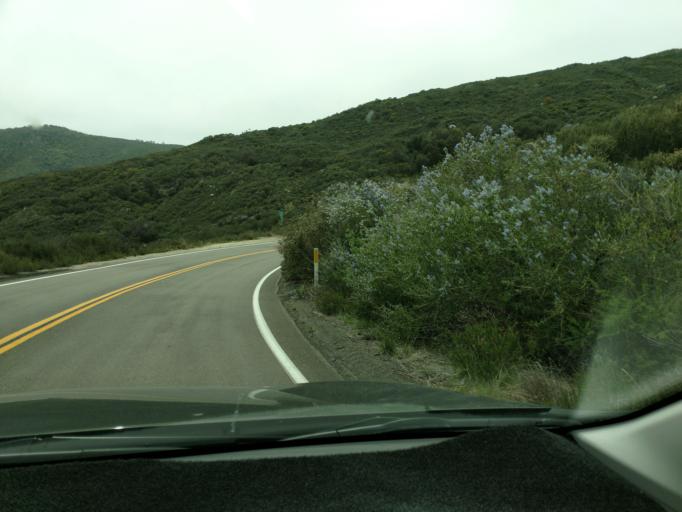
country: US
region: California
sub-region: Riverside County
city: Aguanga
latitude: 33.2514
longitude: -116.7639
